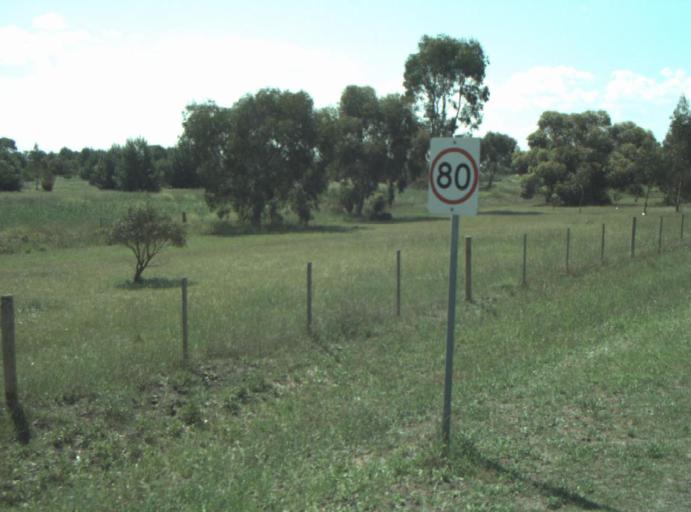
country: AU
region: Victoria
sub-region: Greater Geelong
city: Lara
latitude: -38.0134
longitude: 144.3980
